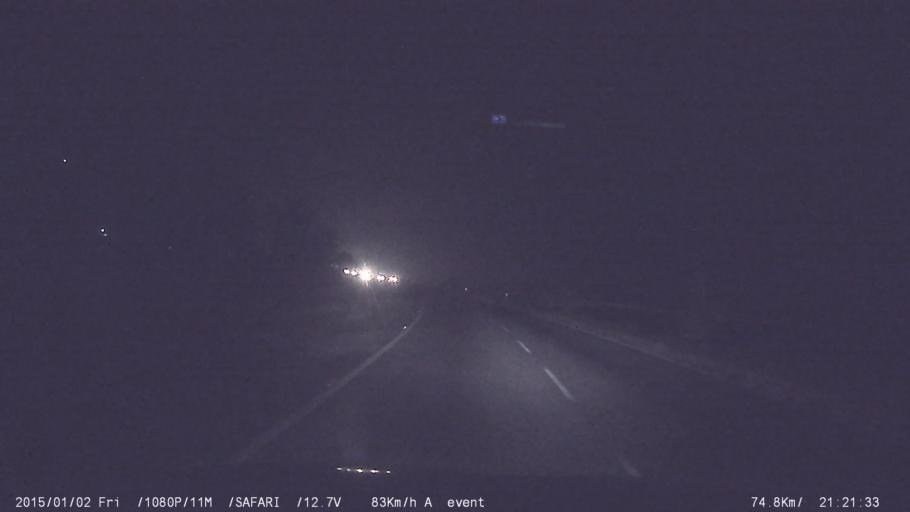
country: IN
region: Tamil Nadu
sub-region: Kancheepuram
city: Kanchipuram
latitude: 12.8893
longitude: 79.5948
